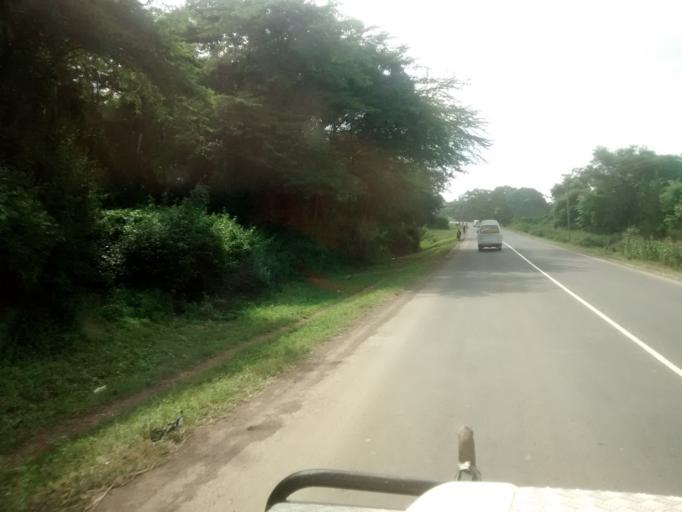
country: TZ
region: Arusha
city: Usa River
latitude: -3.3751
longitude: 36.8307
